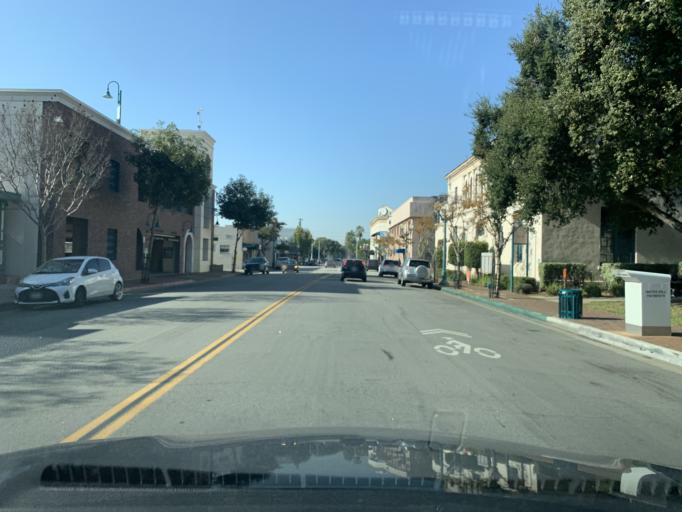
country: US
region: California
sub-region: Los Angeles County
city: Covina
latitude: 34.0875
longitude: -117.8890
